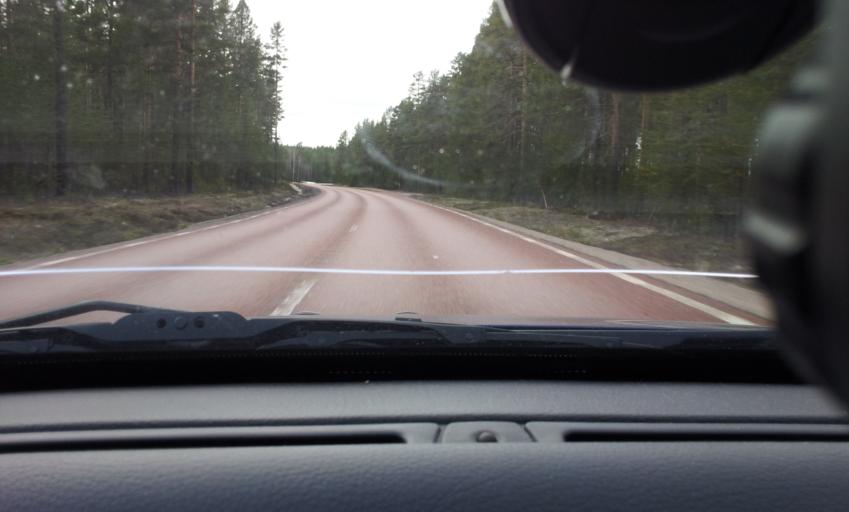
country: SE
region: Gaevleborg
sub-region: Ljusdals Kommun
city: Farila
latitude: 61.8991
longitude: 15.6494
